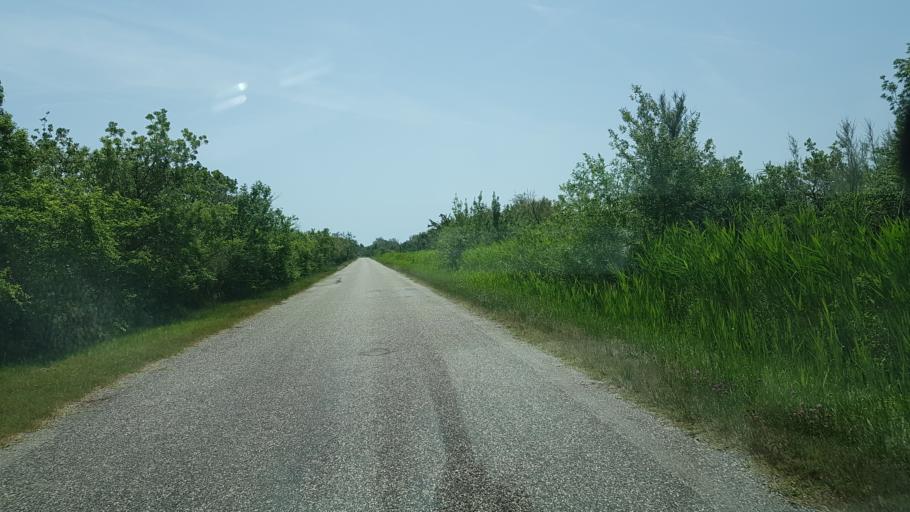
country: FR
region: Provence-Alpes-Cote d'Azur
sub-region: Departement des Bouches-du-Rhone
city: Port-Saint-Louis-du-Rhone
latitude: 43.4658
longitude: 4.6514
